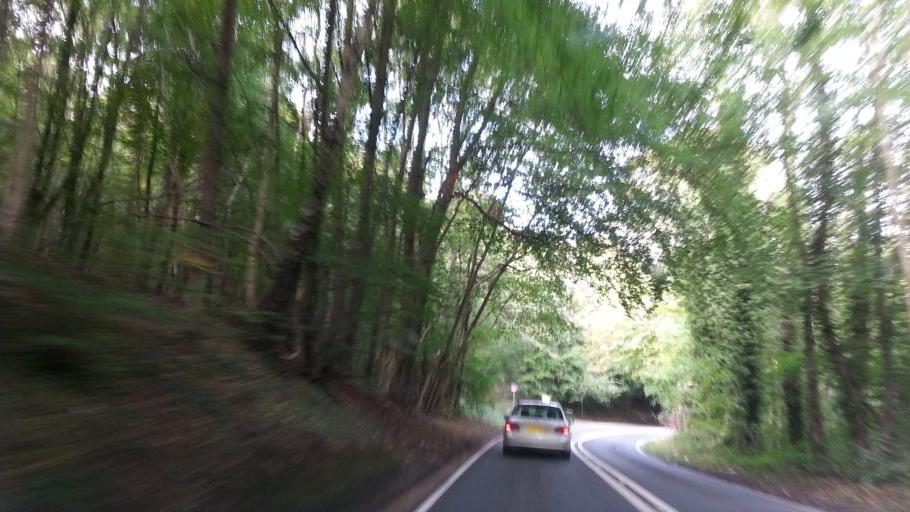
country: GB
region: England
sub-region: Gloucestershire
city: Painswick
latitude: 51.7992
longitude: -2.1909
